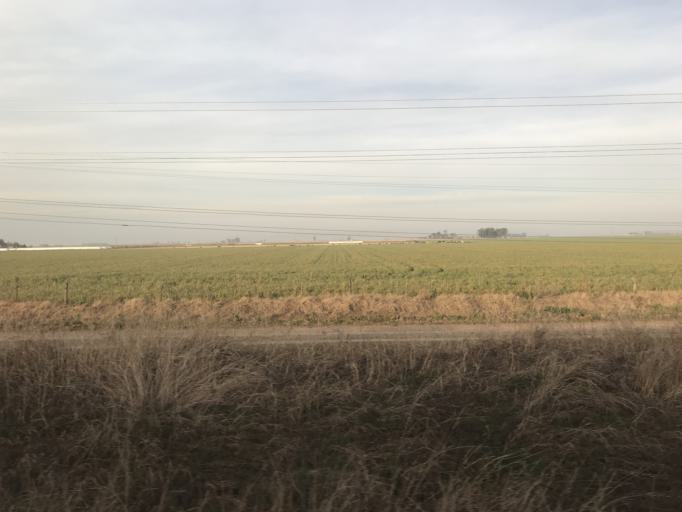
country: AR
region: Cordoba
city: Leones
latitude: -32.6820
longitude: -62.2027
